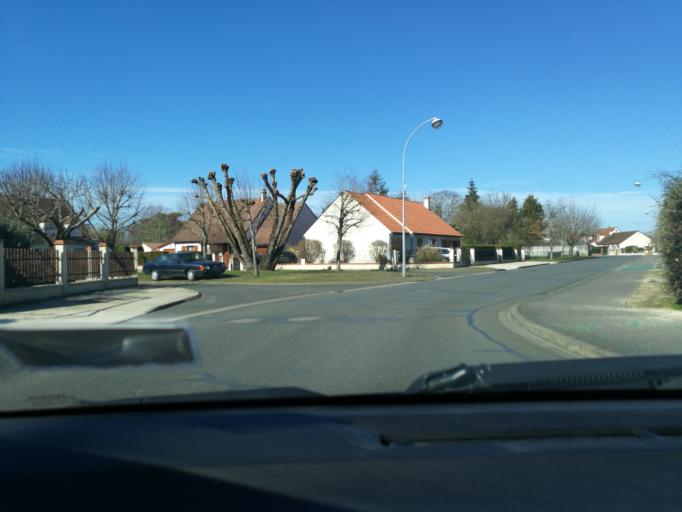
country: FR
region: Centre
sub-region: Departement du Loiret
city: Saint-Jean-le-Blanc
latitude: 47.8848
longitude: 1.9181
